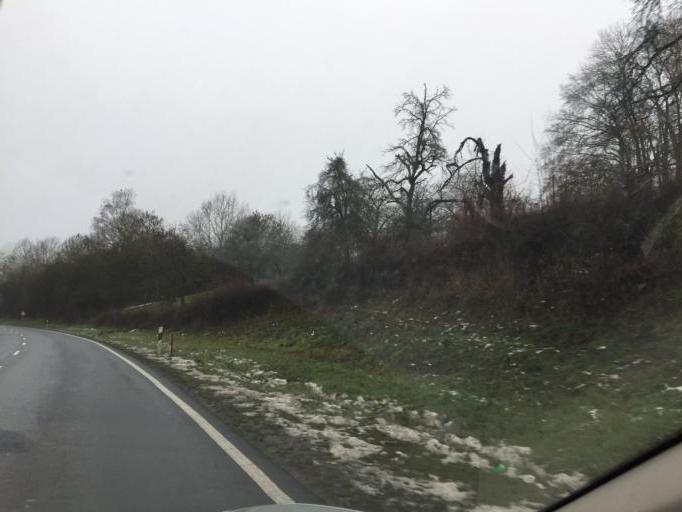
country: LU
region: Diekirch
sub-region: Canton de Diekirch
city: Niederfeulen
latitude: 49.8502
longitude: 6.0679
